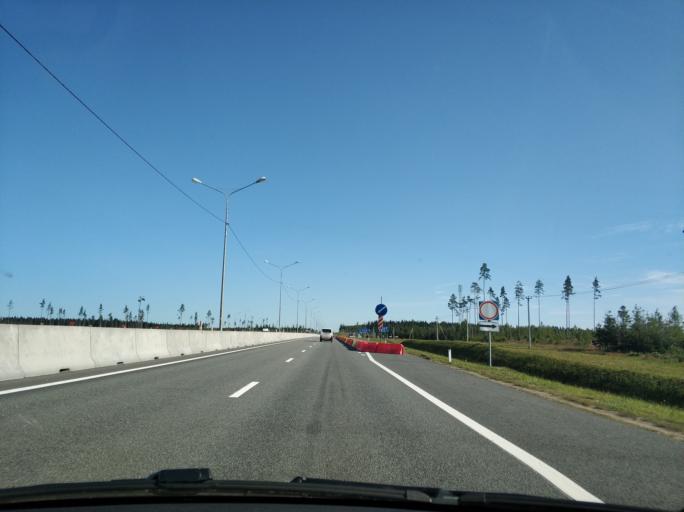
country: RU
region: Leningrad
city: Sosnovo
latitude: 60.4728
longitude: 30.1960
